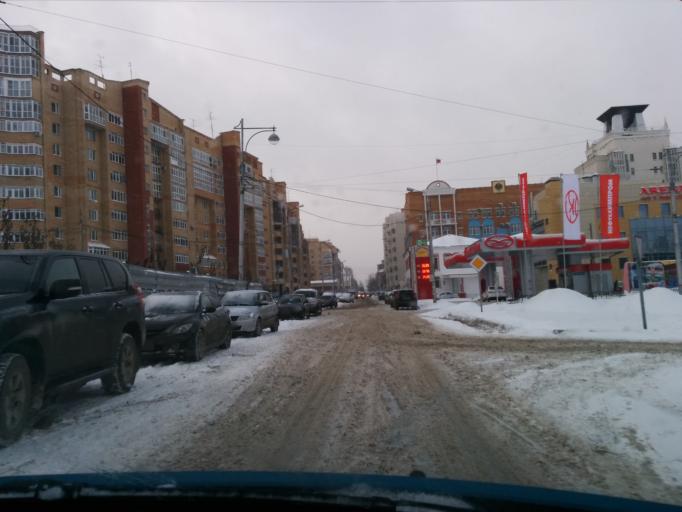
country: RU
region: Perm
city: Perm
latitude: 58.0164
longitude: 56.2610
